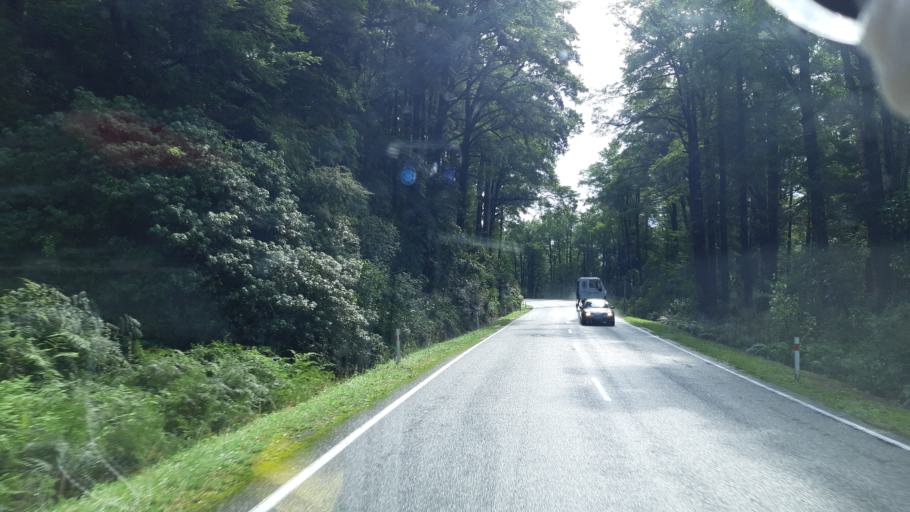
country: NZ
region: West Coast
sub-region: Buller District
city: Westport
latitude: -42.3546
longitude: 172.2397
